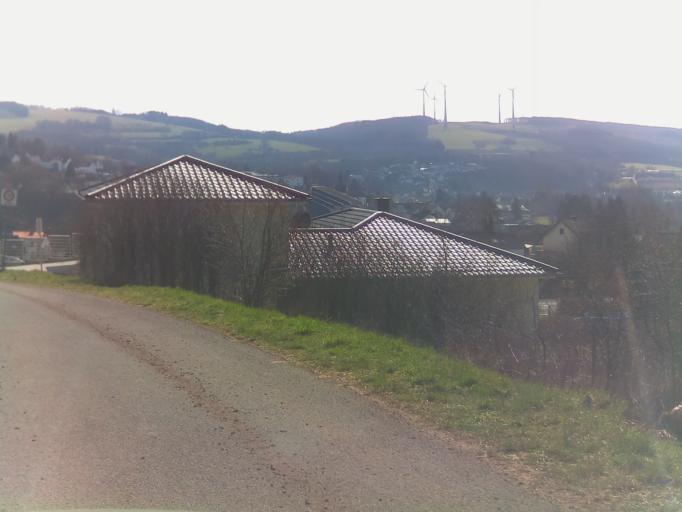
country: DE
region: Saarland
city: Nonnweiler
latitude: 49.5430
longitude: 6.9809
